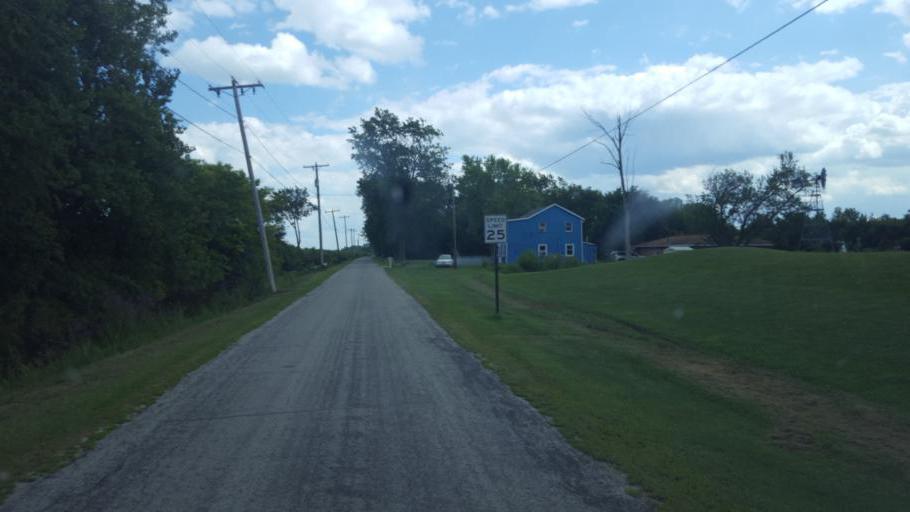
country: US
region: Ohio
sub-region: Lucas County
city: Curtice
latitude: 41.6718
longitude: -83.2785
